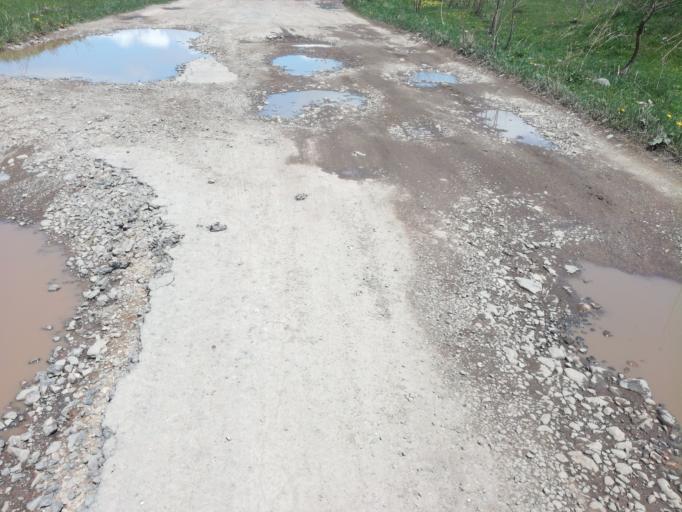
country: AM
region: Lorri
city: Urrut
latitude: 41.1154
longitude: 44.4255
